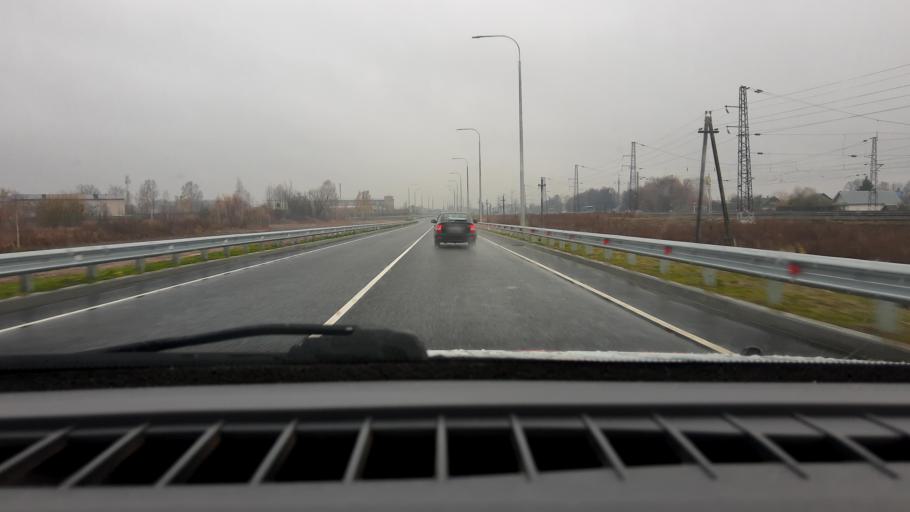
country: RU
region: Nizjnij Novgorod
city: Neklyudovo
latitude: 56.4112
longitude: 43.9834
